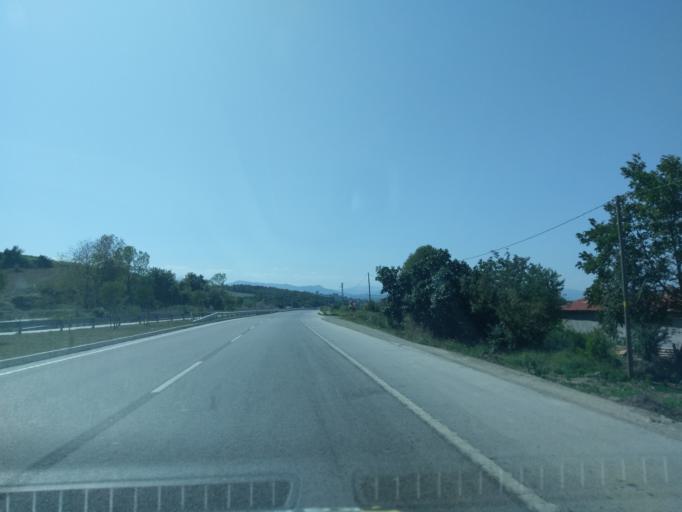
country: TR
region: Samsun
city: Alacam
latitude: 41.6109
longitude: 35.6994
